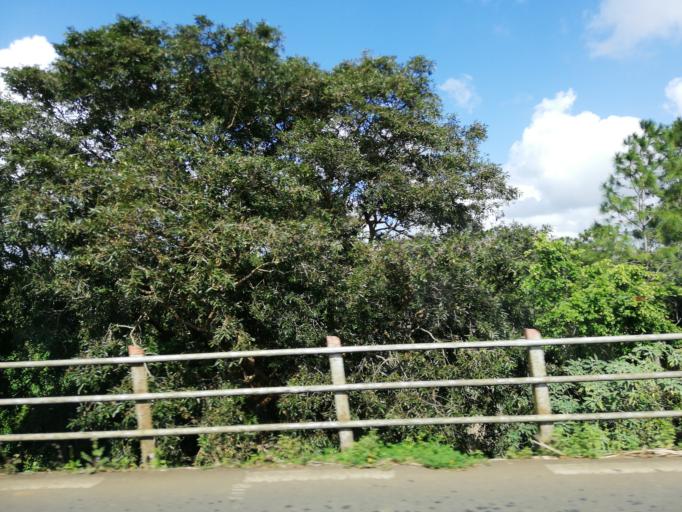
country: MU
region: Moka
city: Verdun
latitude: -20.2130
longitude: 57.5545
